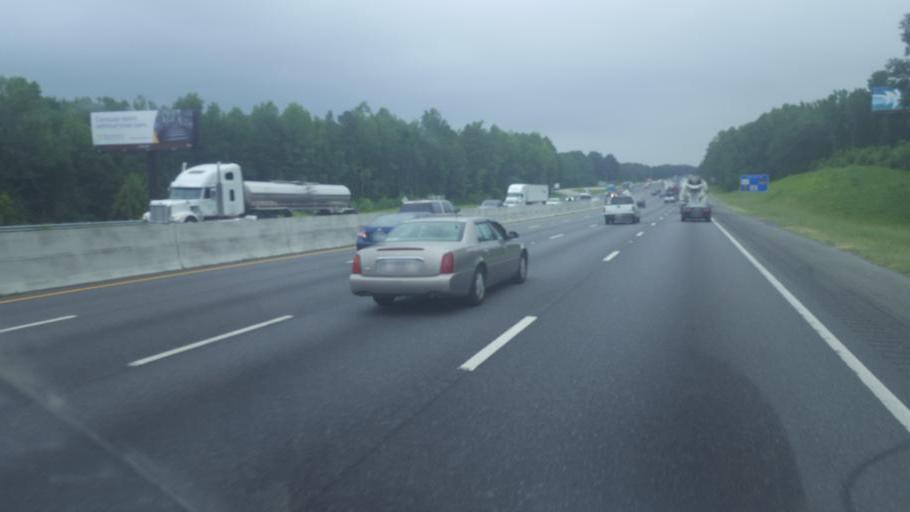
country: US
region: South Carolina
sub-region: York County
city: Fort Mill
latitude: 35.0113
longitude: -80.9702
